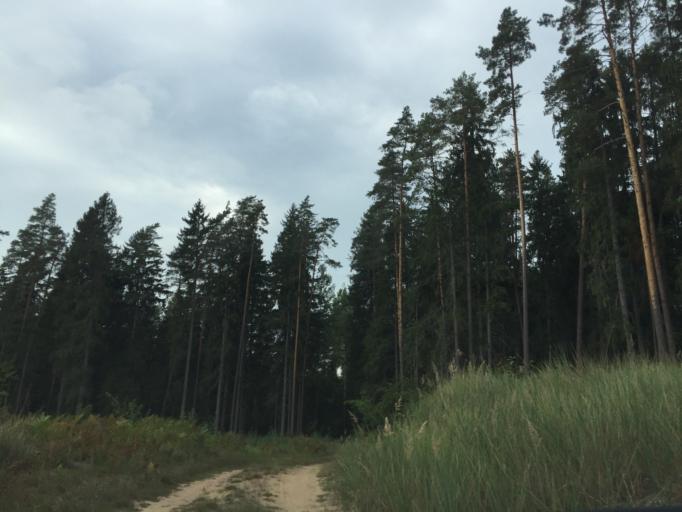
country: LV
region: Baldone
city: Baldone
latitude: 56.7755
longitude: 24.4454
